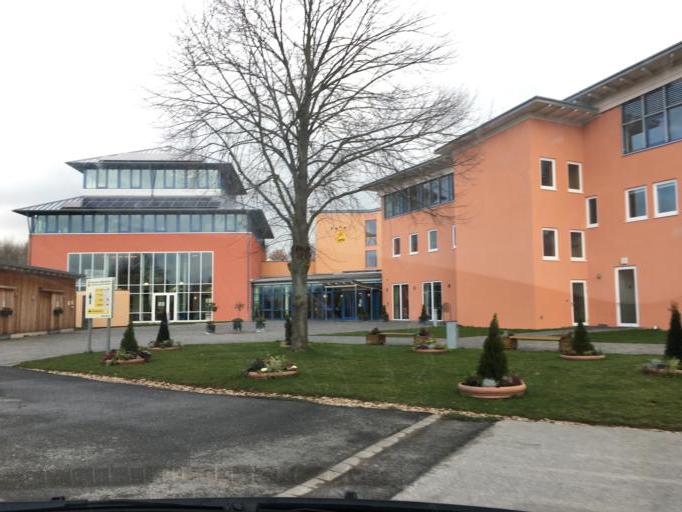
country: DE
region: North Rhine-Westphalia
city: Julich
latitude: 50.9240
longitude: 6.3425
